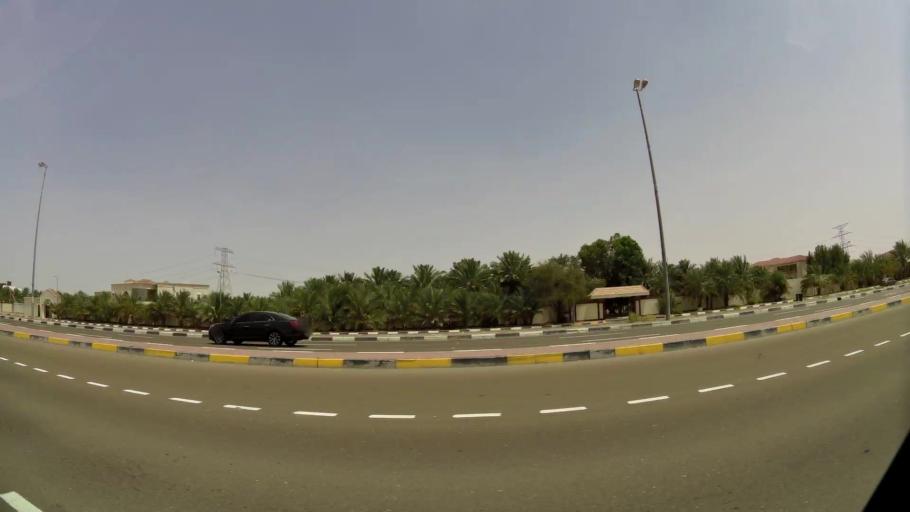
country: AE
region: Abu Dhabi
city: Al Ain
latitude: 24.1880
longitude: 55.6877
